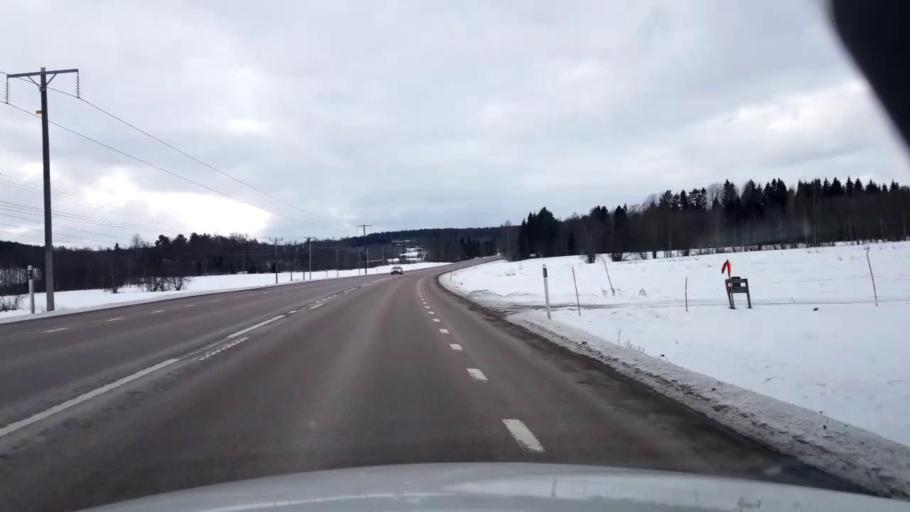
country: SE
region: Gaevleborg
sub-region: Nordanstigs Kommun
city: Bergsjoe
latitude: 62.0162
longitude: 17.2502
